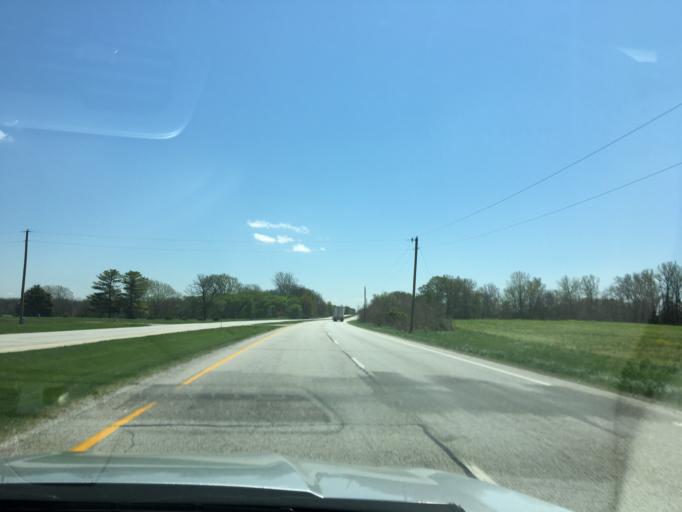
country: US
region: Indiana
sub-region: Boone County
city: Thorntown
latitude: 40.2173
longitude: -86.6587
